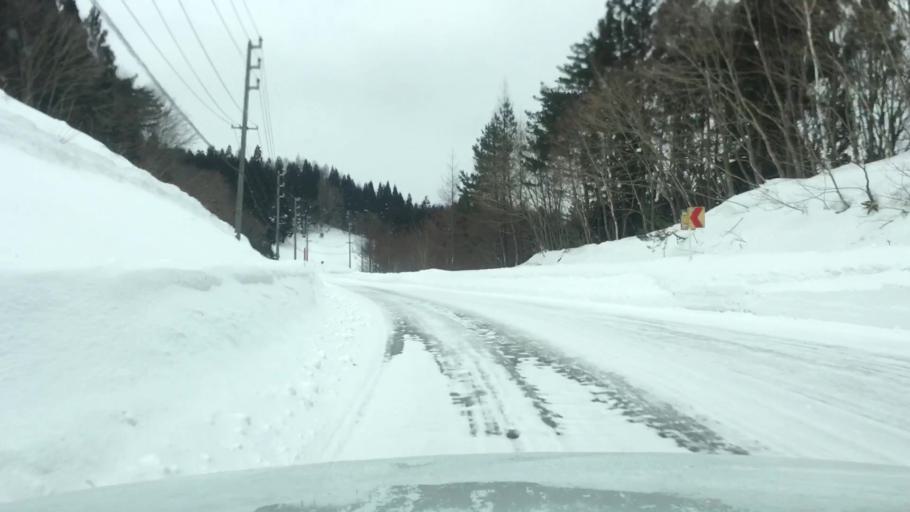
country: JP
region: Akita
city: Hanawa
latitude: 39.9996
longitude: 140.9886
